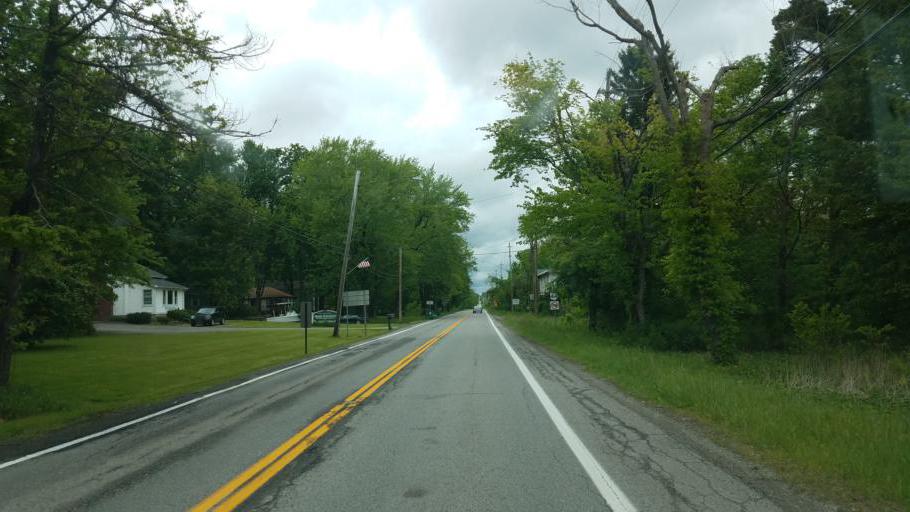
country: US
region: Ohio
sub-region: Portage County
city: Mantua
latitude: 41.3876
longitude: -81.2163
